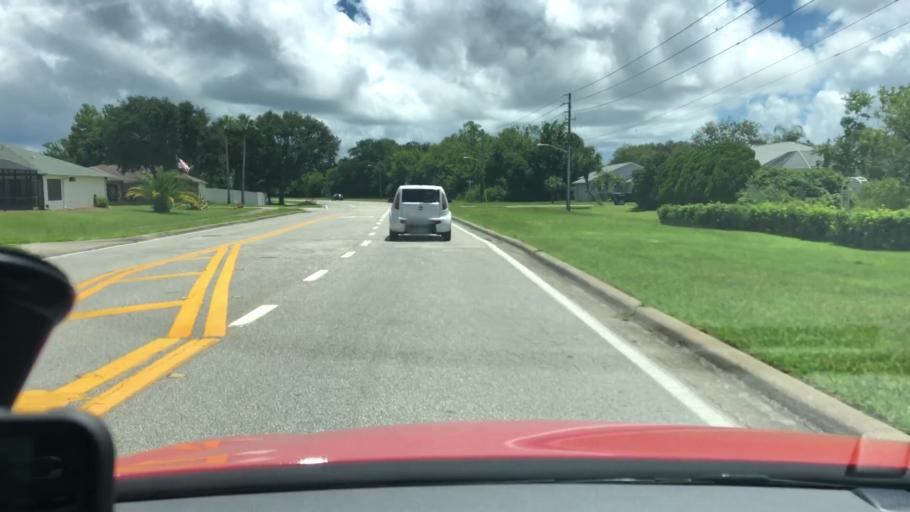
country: US
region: Florida
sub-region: Volusia County
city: South Daytona
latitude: 29.1416
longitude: -81.0438
